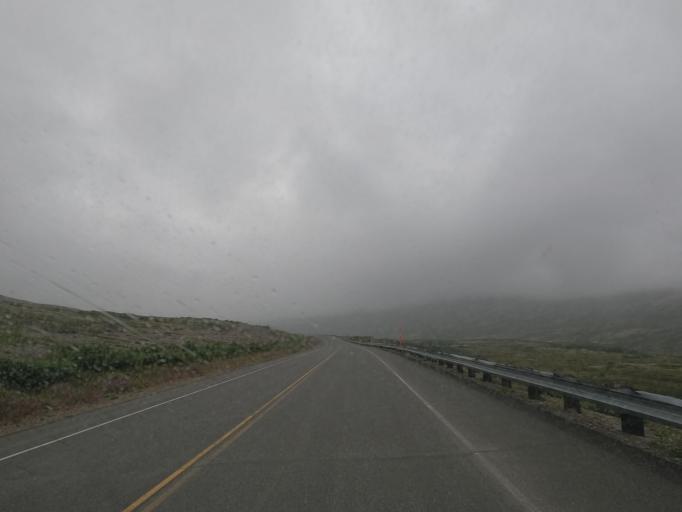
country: US
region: Alaska
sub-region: Haines Borough
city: Haines
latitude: 59.6760
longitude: -136.5691
